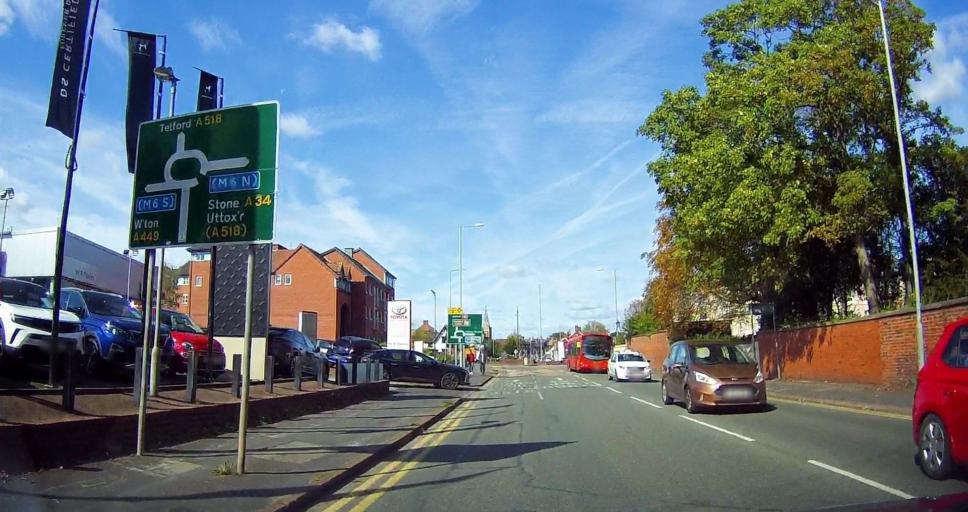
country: GB
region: England
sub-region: Staffordshire
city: Stafford
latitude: 52.8022
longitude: -2.1111
